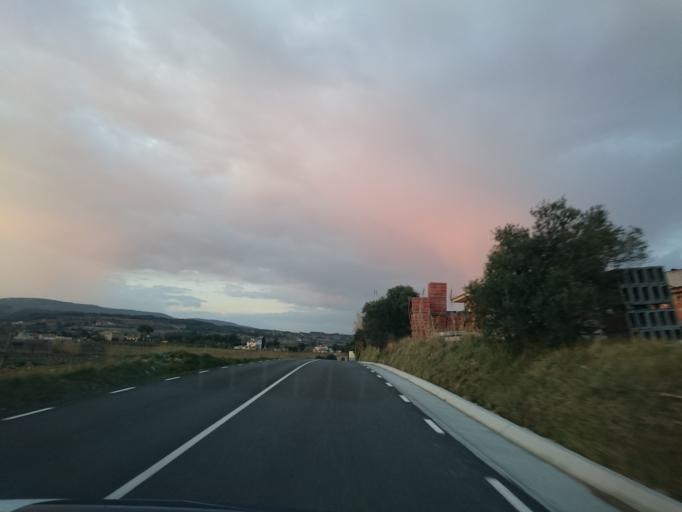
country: ES
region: Catalonia
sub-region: Provincia de Barcelona
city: Sant Marti Sarroca
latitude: 41.3884
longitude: 1.5969
